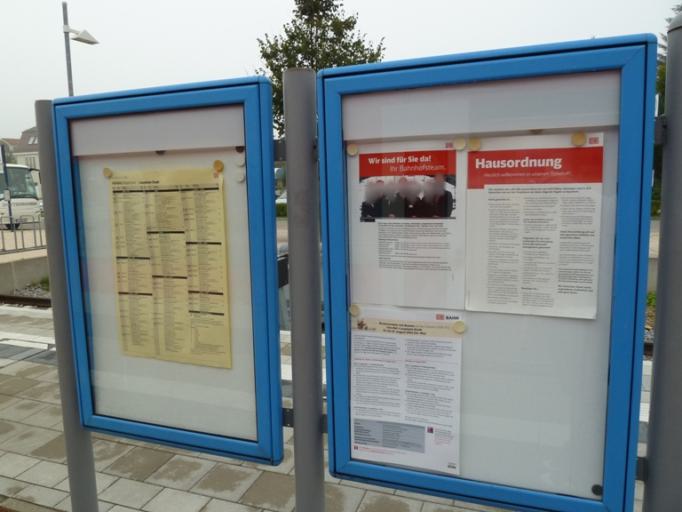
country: DE
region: Baden-Wuerttemberg
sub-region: Tuebingen Region
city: Laupheim
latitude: 48.2338
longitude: 9.8786
